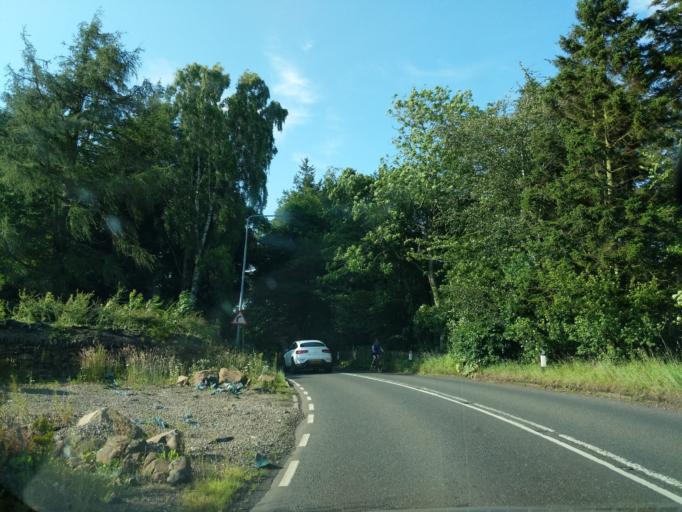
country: GB
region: Scotland
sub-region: Edinburgh
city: Balerno
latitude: 55.8856
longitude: -3.3524
